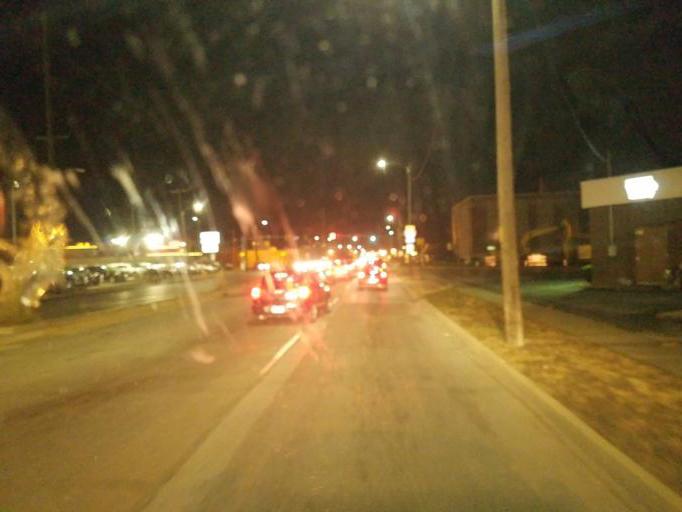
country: US
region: Iowa
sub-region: Polk County
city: Des Moines
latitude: 41.6004
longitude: -93.5798
